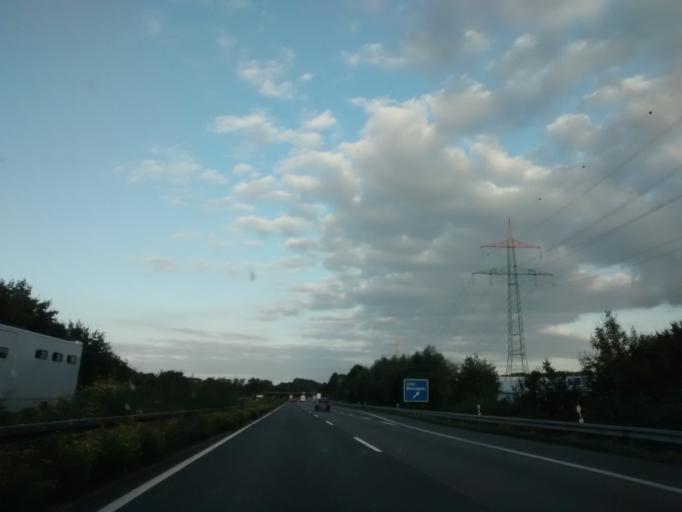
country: DE
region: North Rhine-Westphalia
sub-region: Regierungsbezirk Munster
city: Lotte
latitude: 52.2649
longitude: 7.8861
